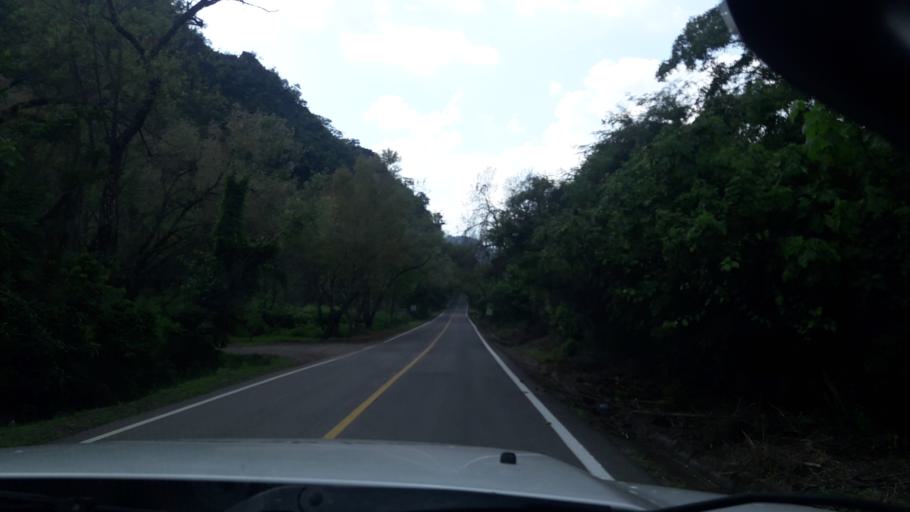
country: MX
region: Colima
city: Suchitlan
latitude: 19.4511
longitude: -103.7151
